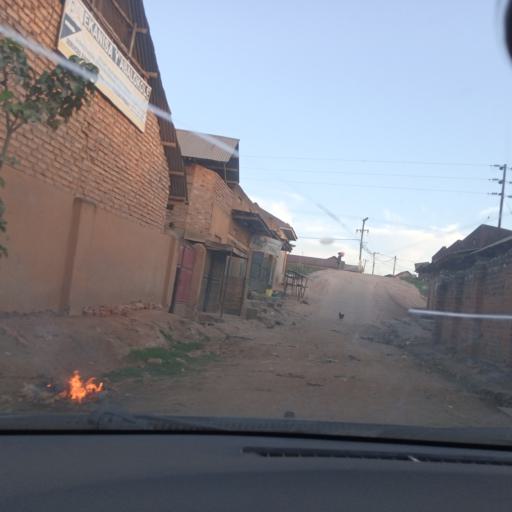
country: UG
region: Central Region
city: Masaka
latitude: -0.3230
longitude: 31.7590
